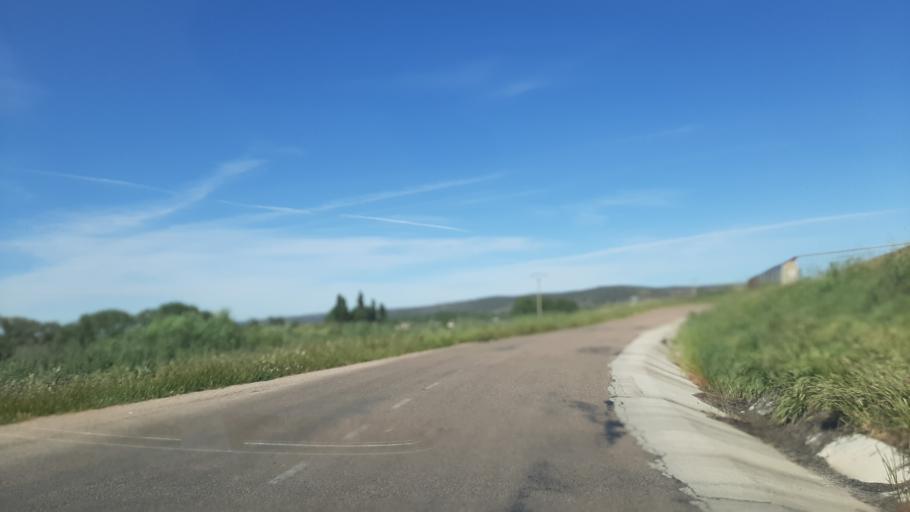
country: ES
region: Castille and Leon
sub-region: Provincia de Salamanca
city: Alba de Tormes
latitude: 40.8196
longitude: -5.4948
